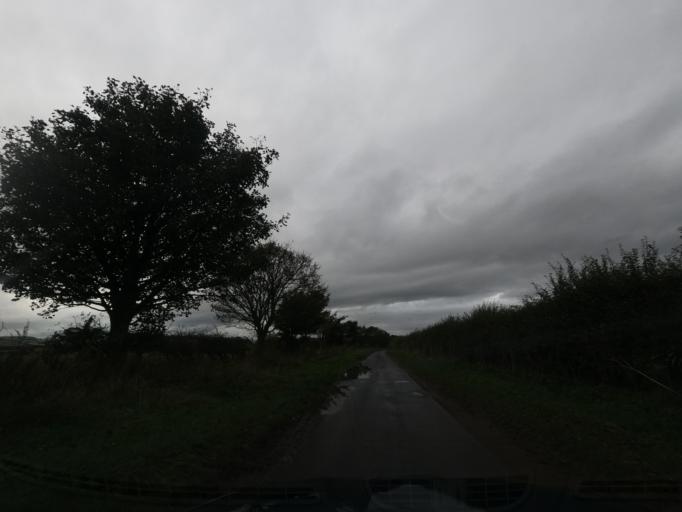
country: GB
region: England
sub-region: Northumberland
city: Doddington
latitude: 55.5906
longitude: -2.0115
